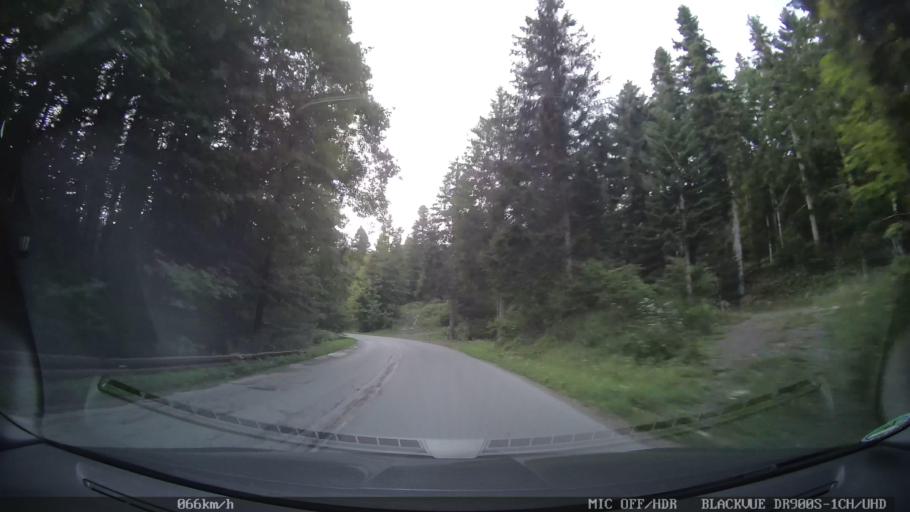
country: HR
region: Primorsko-Goranska
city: Vrbovsko
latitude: 45.2386
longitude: 15.0731
